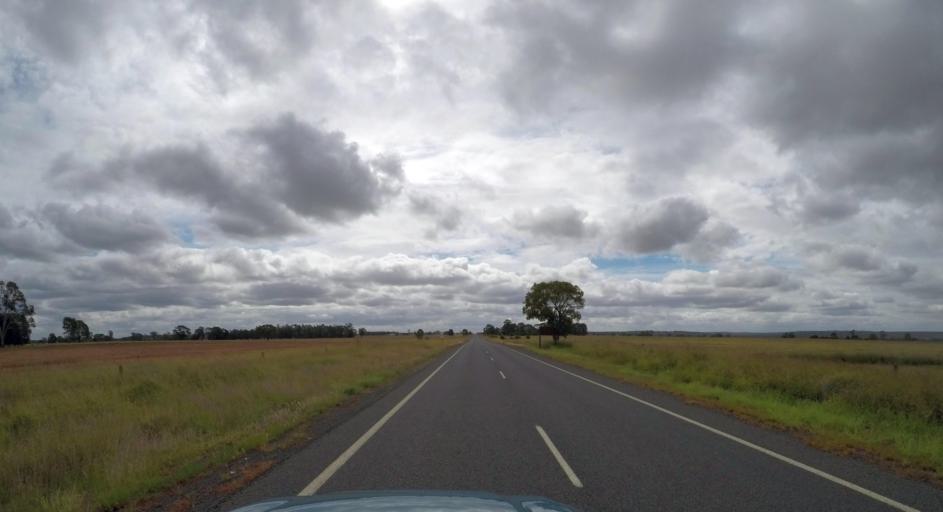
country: AU
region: Queensland
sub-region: South Burnett
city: Kingaroy
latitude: -26.3884
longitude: 151.2447
